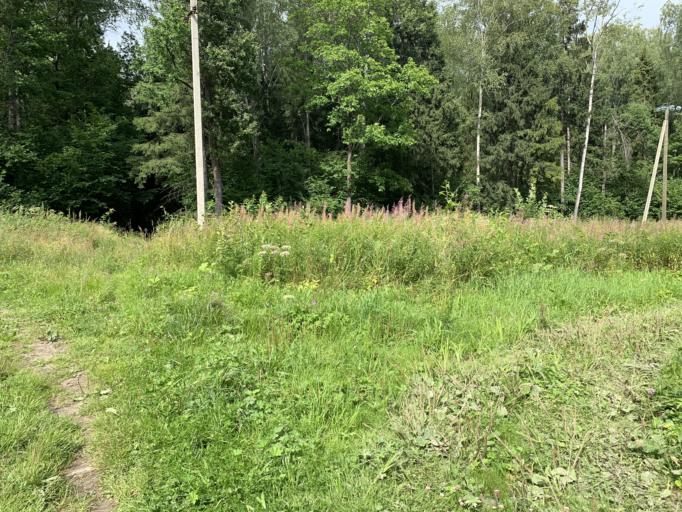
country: RU
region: Moskovskaya
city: Podosinki
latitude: 56.1818
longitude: 37.5680
